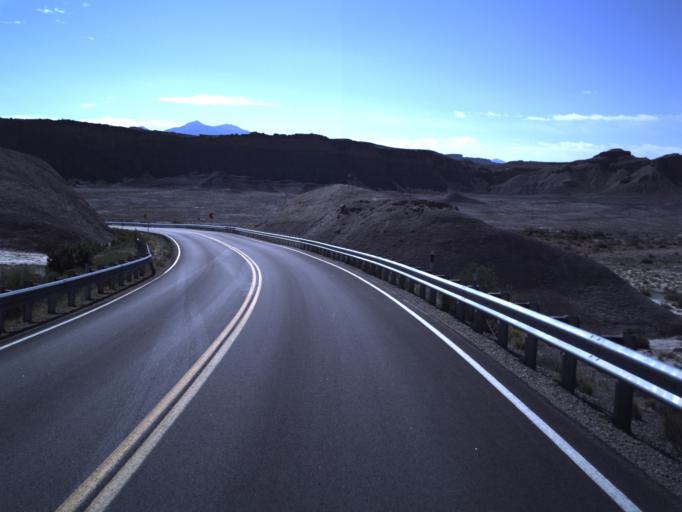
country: US
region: Utah
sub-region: Wayne County
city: Loa
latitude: 38.2689
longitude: -111.0805
